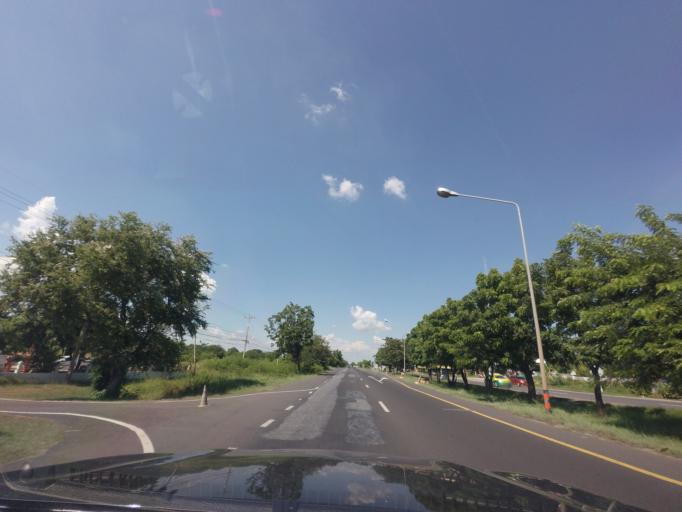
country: TH
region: Nakhon Ratchasima
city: Non Sung
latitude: 15.1957
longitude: 102.3496
